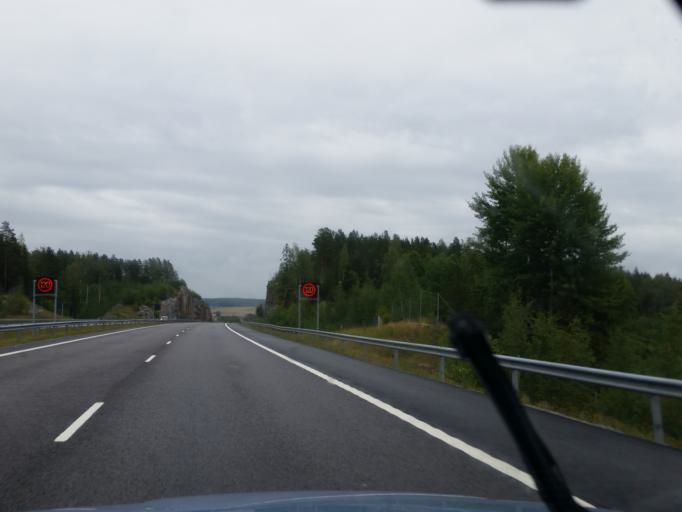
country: FI
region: Varsinais-Suomi
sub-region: Salo
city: Halikko
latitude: 60.4335
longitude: 22.9852
